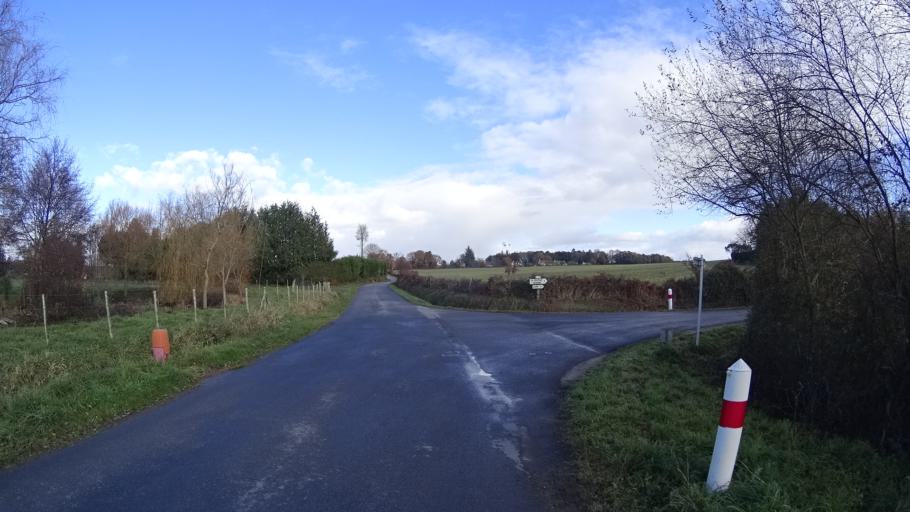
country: FR
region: Brittany
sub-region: Departement du Morbihan
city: La Gacilly
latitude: 47.7902
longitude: -2.1519
